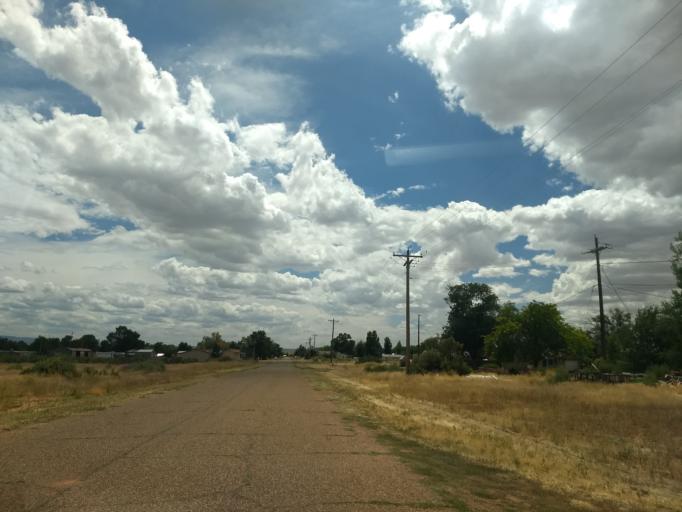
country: US
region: Arizona
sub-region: Coconino County
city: Fredonia
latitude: 36.9562
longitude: -112.5243
